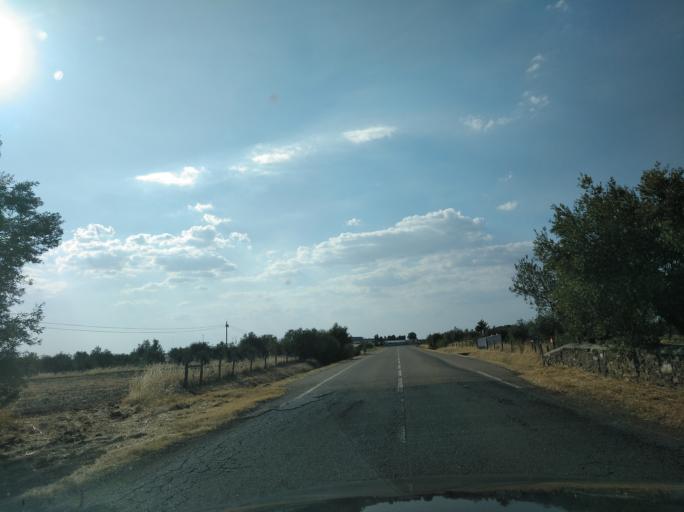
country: PT
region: Evora
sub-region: Mourao
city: Mourao
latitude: 38.3775
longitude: -7.3287
